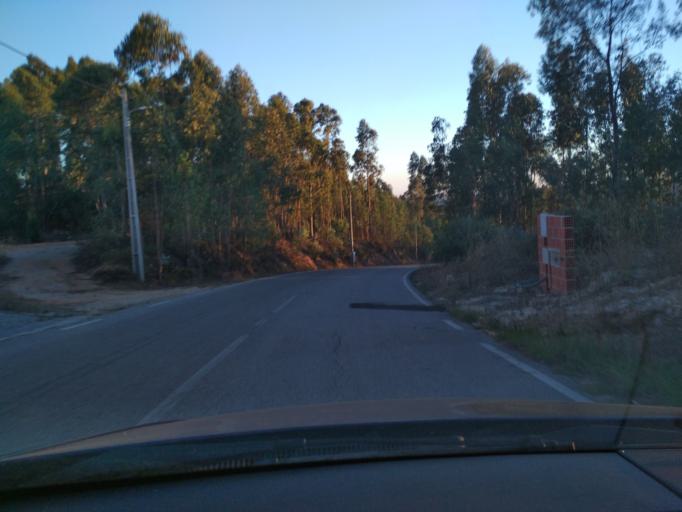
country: PT
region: Coimbra
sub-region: Coimbra
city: Coimbra
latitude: 40.1784
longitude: -8.4766
